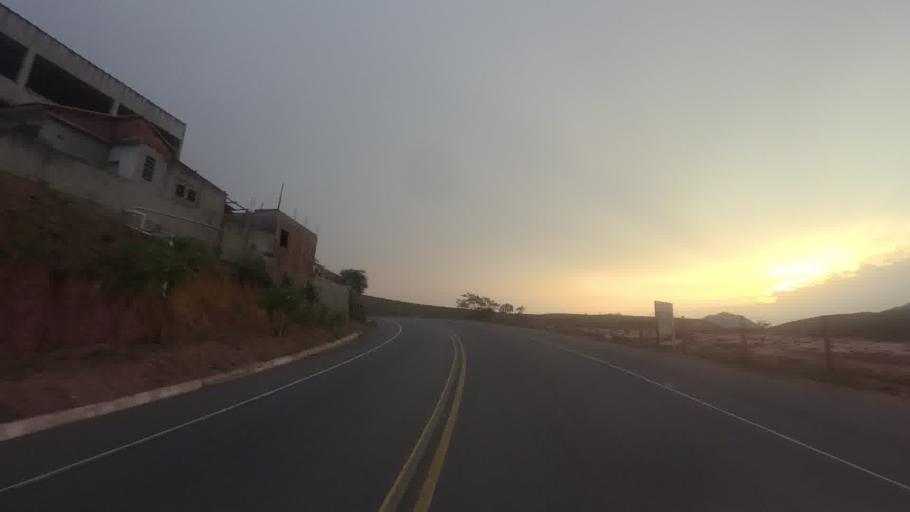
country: BR
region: Minas Gerais
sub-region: Recreio
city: Recreio
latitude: -21.7463
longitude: -42.4642
